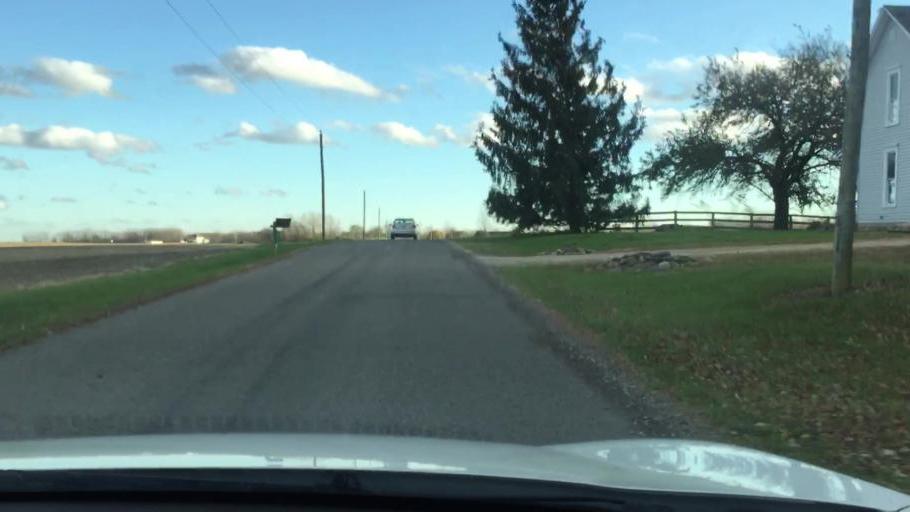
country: US
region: Ohio
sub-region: Champaign County
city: North Lewisburg
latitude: 40.2354
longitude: -83.5187
